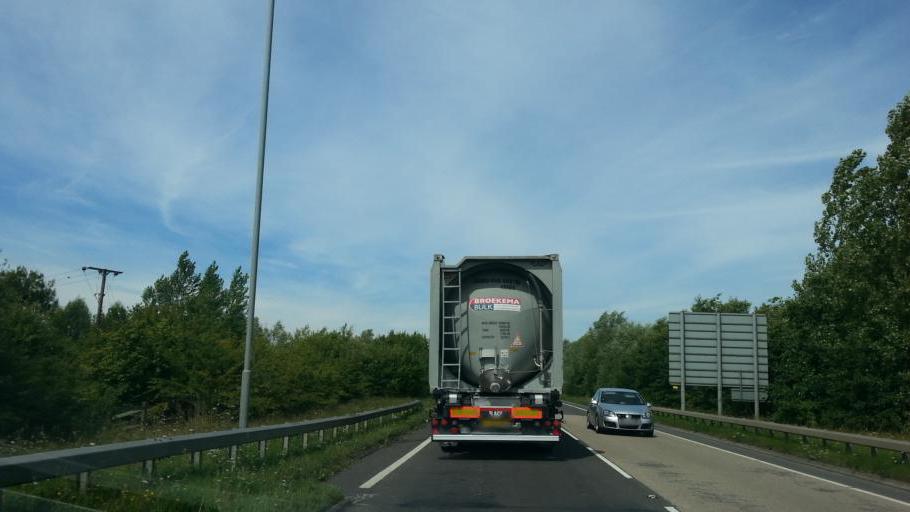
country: GB
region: England
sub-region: Suffolk
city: Exning
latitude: 52.3047
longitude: 0.3731
